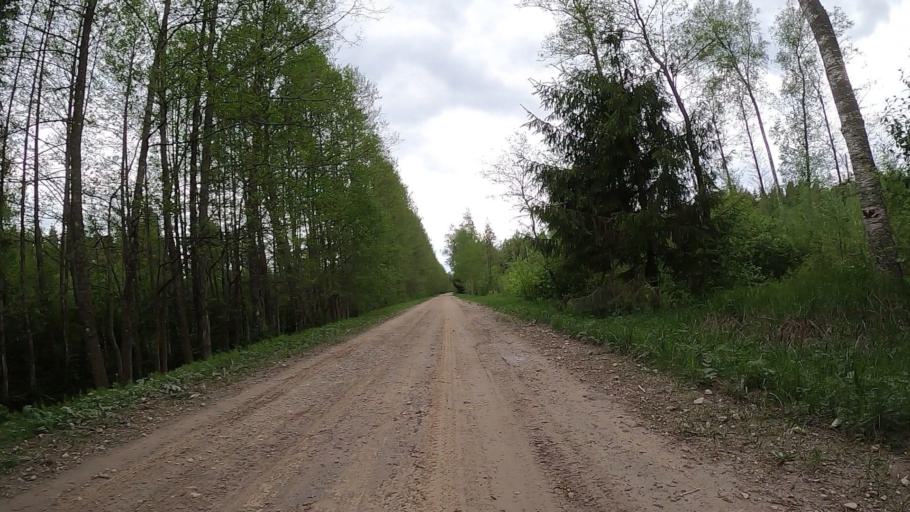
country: LV
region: Ozolnieku
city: Ozolnieki
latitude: 56.7880
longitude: 23.7748
